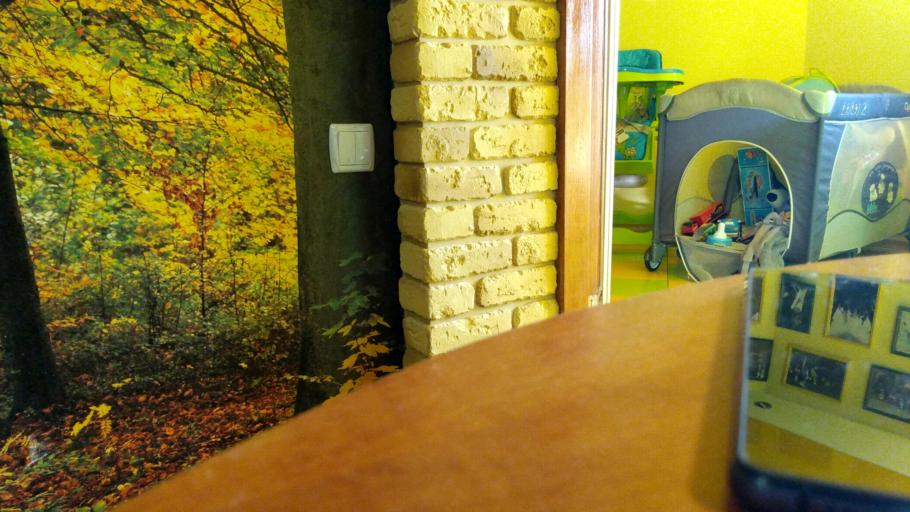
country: RU
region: Tverskaya
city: Kalashnikovo
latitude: 57.2919
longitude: 35.3528
